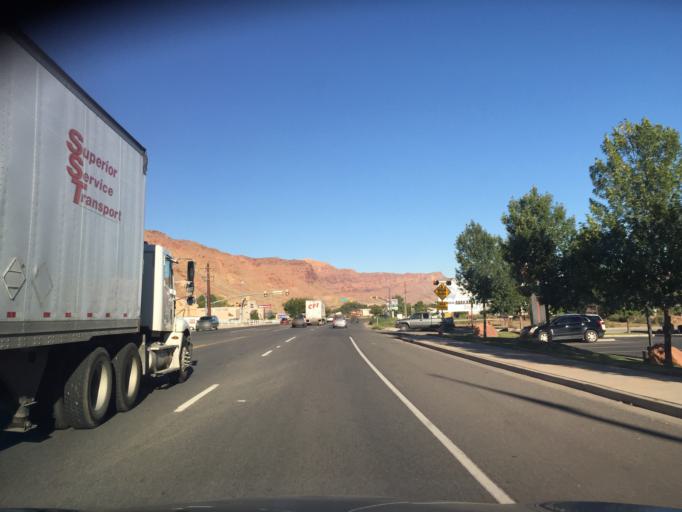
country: US
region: Utah
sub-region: Grand County
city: Moab
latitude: 38.5570
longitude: -109.5413
